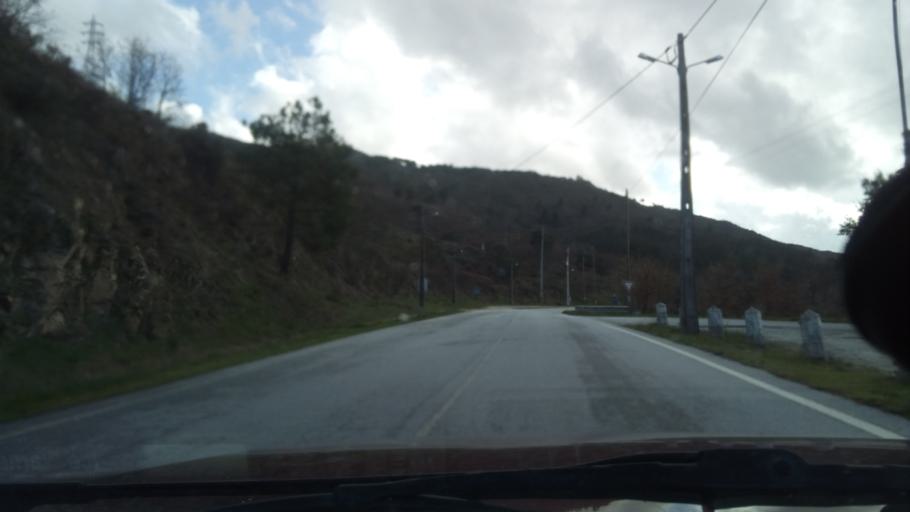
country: PT
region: Guarda
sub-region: Guarda
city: Guarda
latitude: 40.5620
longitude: -7.3004
